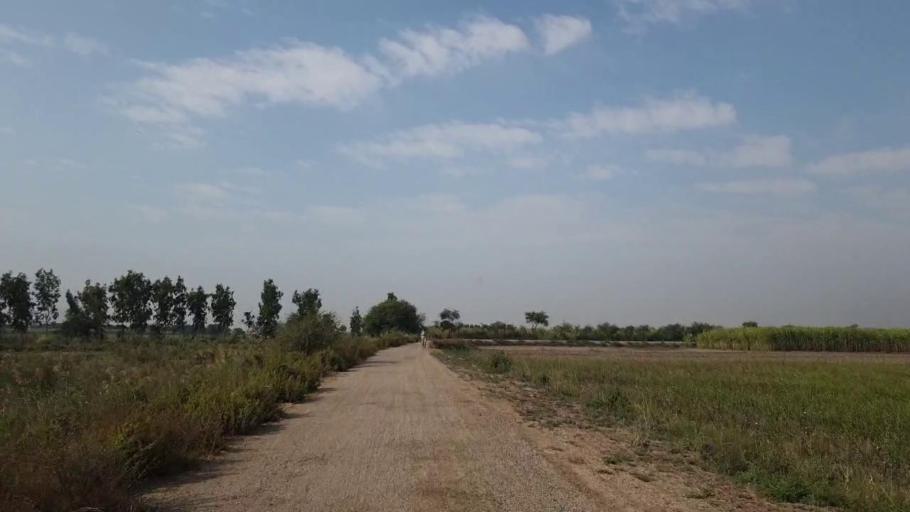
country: PK
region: Sindh
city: Tando Muhammad Khan
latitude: 25.0534
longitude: 68.4321
